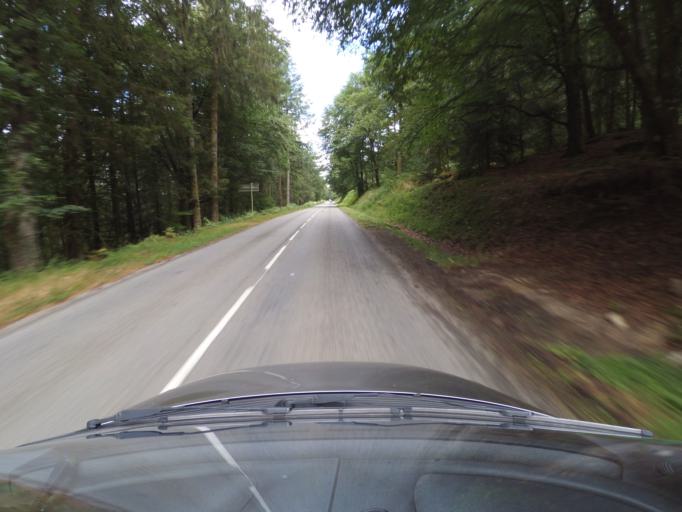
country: FR
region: Limousin
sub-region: Departement de la Creuse
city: Bourganeuf
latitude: 45.8989
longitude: 1.8600
